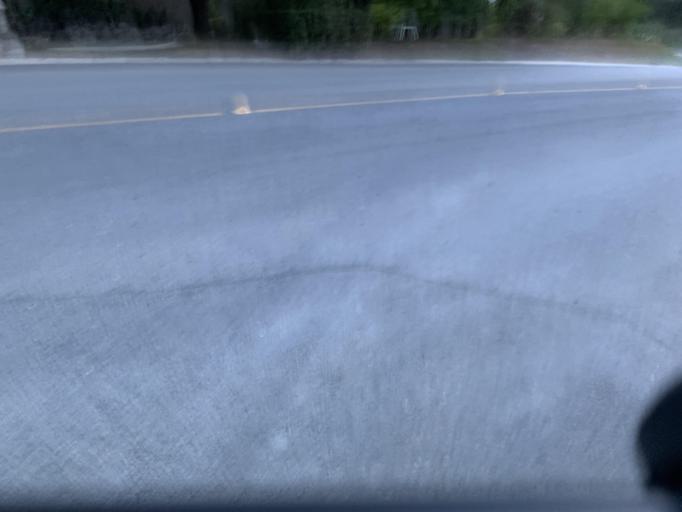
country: MX
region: Nuevo Leon
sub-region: Juarez
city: Bosques de San Pedro
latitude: 25.5191
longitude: -100.1894
